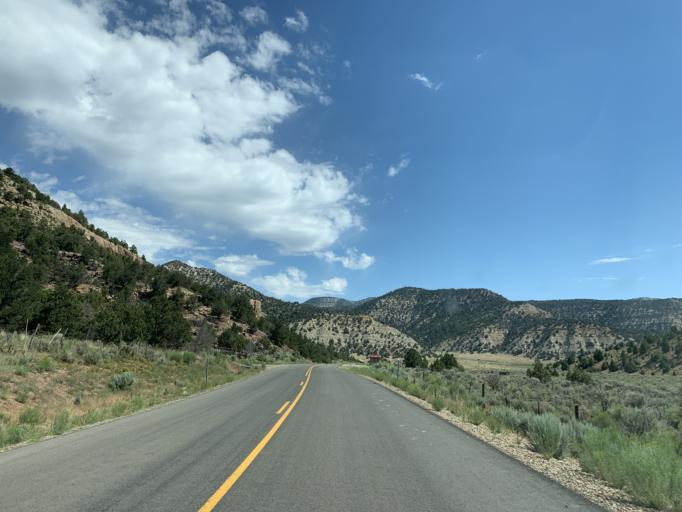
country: US
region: Utah
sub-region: Carbon County
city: East Carbon City
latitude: 39.7688
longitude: -110.5179
